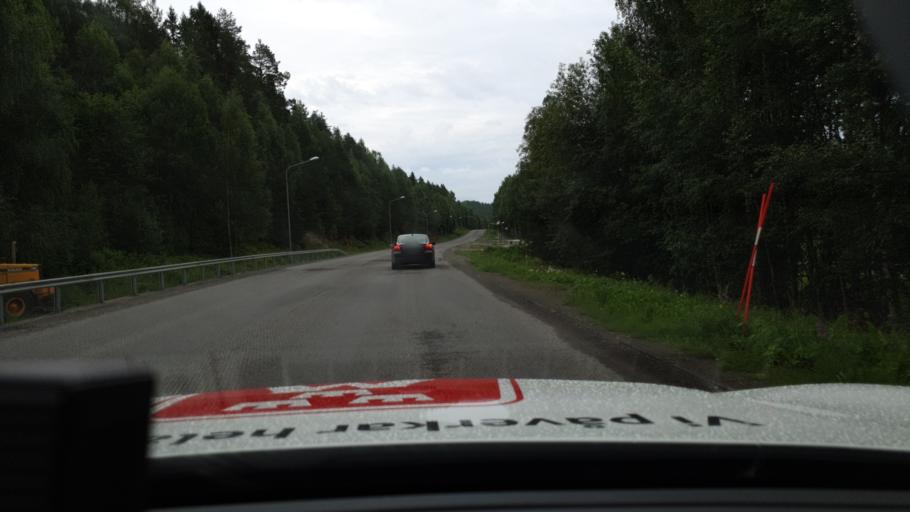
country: SE
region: Norrbotten
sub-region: Bodens Kommun
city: Boden
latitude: 65.8451
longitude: 21.5994
